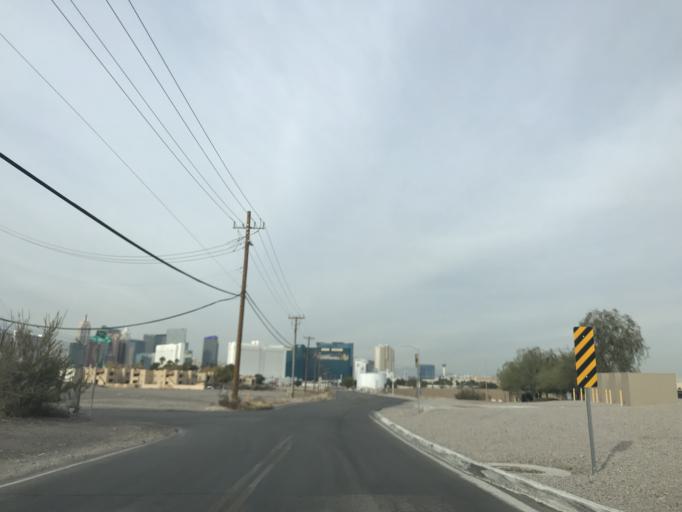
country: US
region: Nevada
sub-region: Clark County
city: Paradise
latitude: 36.0894
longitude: -115.1683
